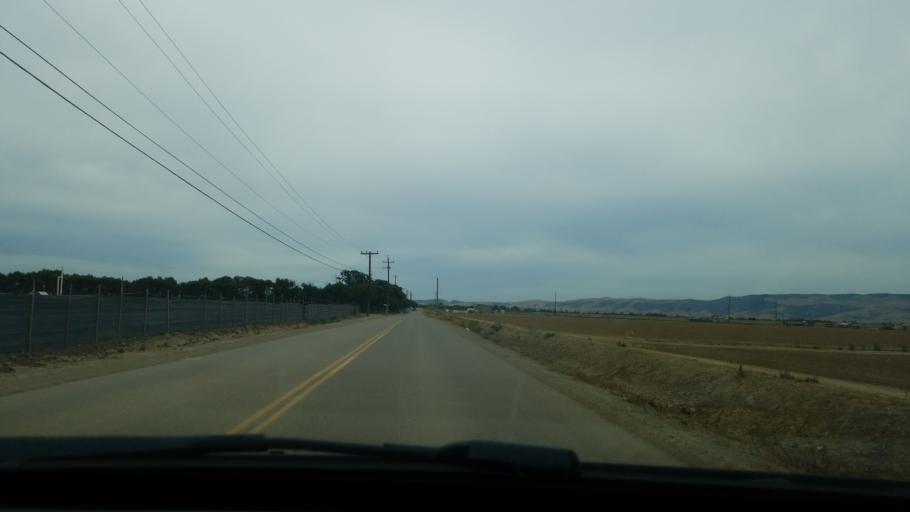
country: US
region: California
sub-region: Santa Barbara County
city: Guadalupe
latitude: 34.9935
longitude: -120.5140
